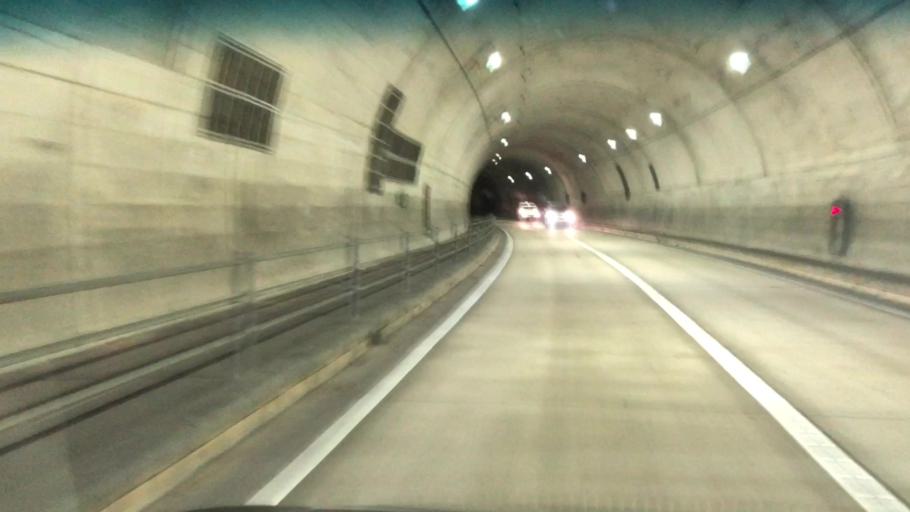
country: JP
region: Nagasaki
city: Sasebo
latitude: 32.9501
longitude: 129.6413
